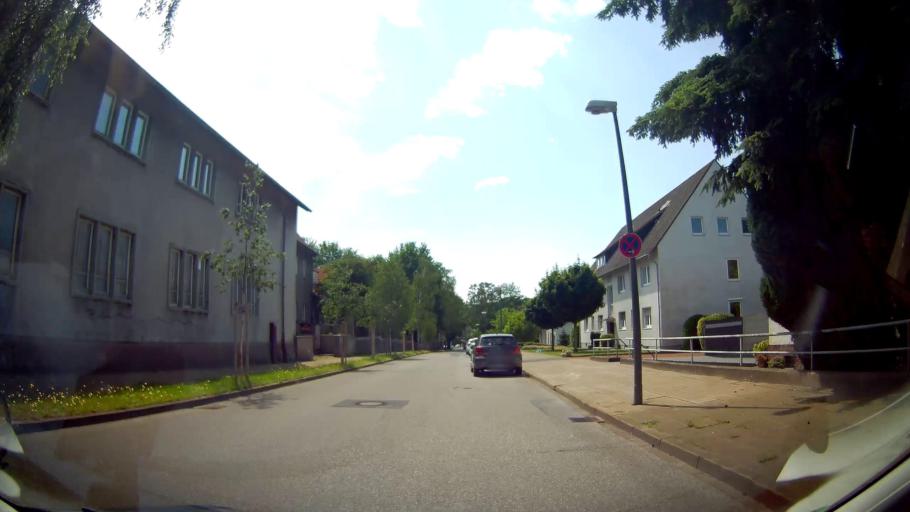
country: DE
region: North Rhine-Westphalia
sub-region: Regierungsbezirk Munster
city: Gladbeck
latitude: 51.5943
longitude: 7.0423
